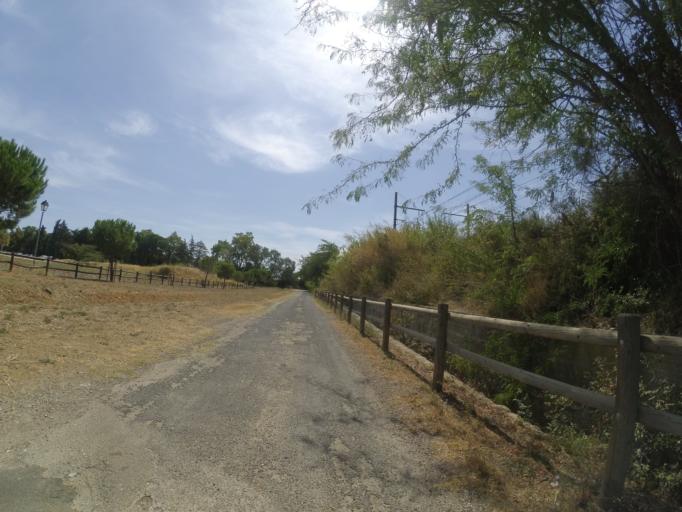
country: FR
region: Languedoc-Roussillon
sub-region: Departement des Pyrenees-Orientales
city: Rivesaltes
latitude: 42.7603
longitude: 2.8707
